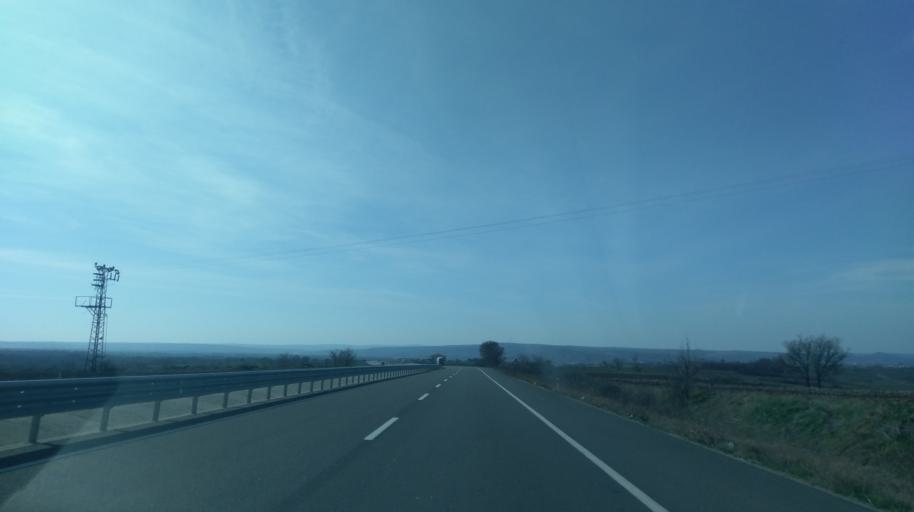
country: TR
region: Edirne
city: Hamidiye
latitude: 41.1398
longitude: 26.6594
